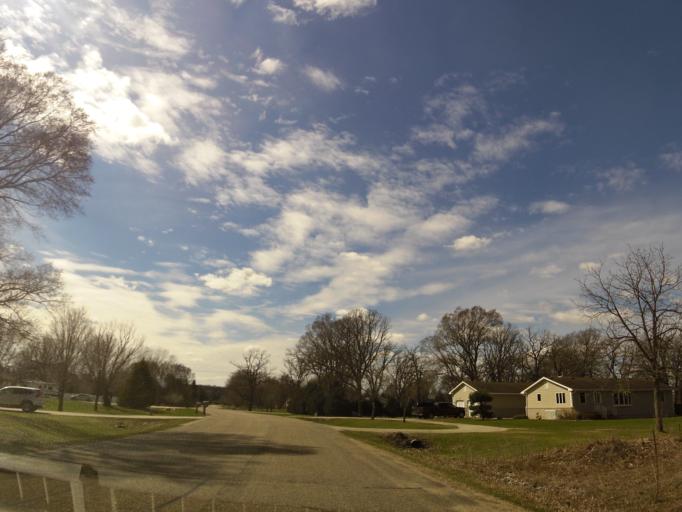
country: US
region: Minnesota
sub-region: Olmsted County
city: Rochester
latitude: 44.0059
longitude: -92.3686
